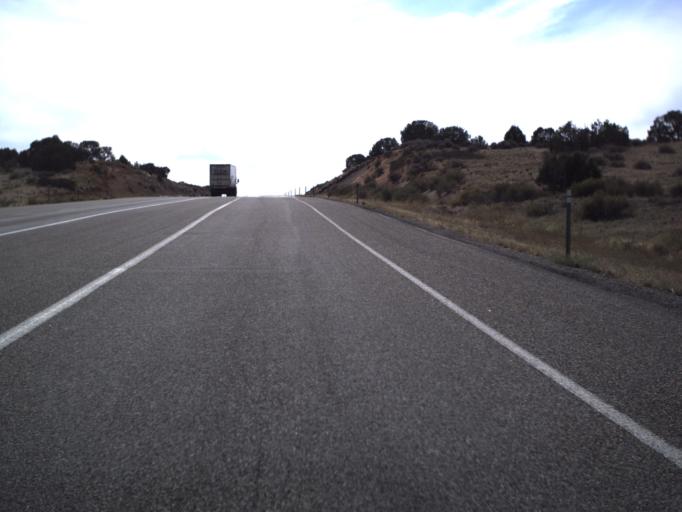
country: US
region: Colorado
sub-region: Mesa County
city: Loma
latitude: 39.1839
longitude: -109.1191
